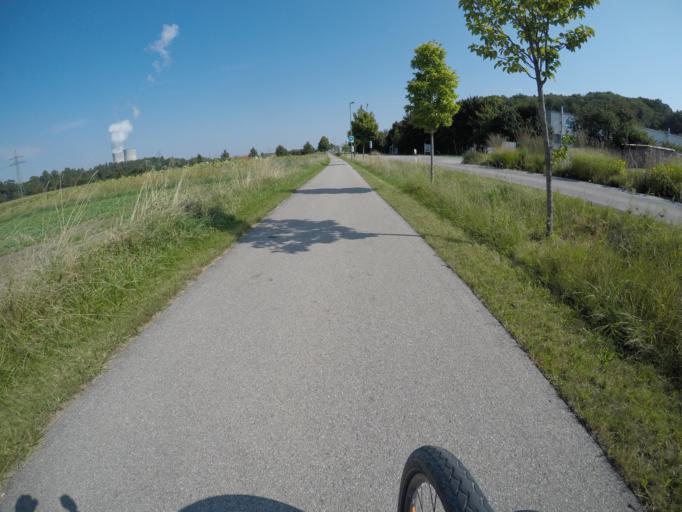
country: DE
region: Bavaria
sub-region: Swabia
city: Gundremmingen
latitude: 48.4951
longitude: 10.3938
